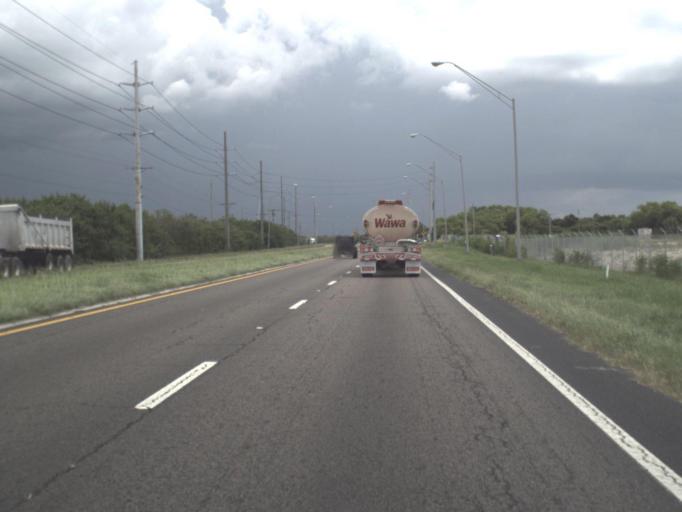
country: US
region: Florida
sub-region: Hillsborough County
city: Tampa
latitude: 27.9264
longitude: -82.4224
